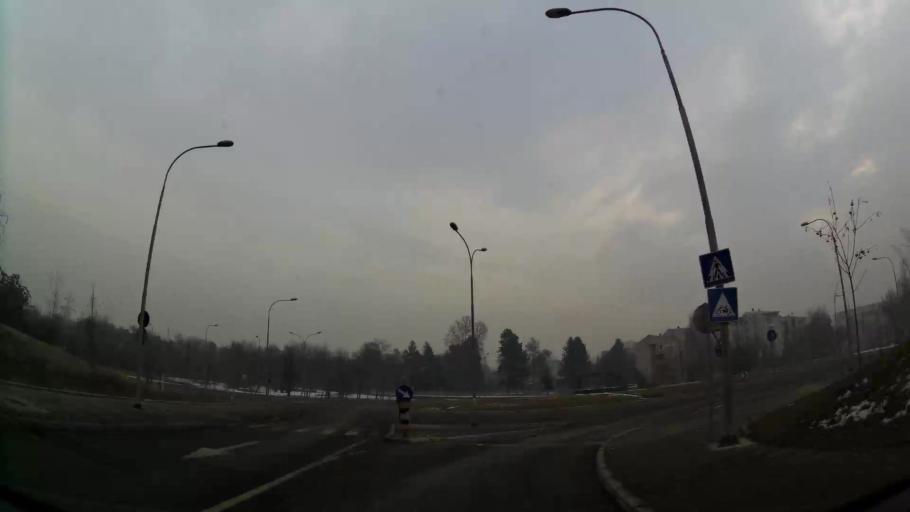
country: MK
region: Cair
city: Cair
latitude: 42.0074
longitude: 21.4629
